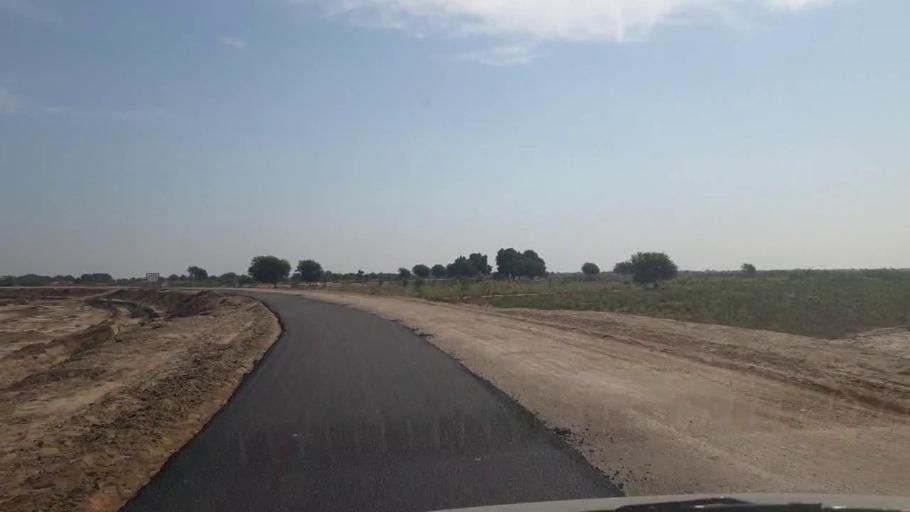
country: PK
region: Sindh
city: Digri
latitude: 24.9725
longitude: 69.1246
